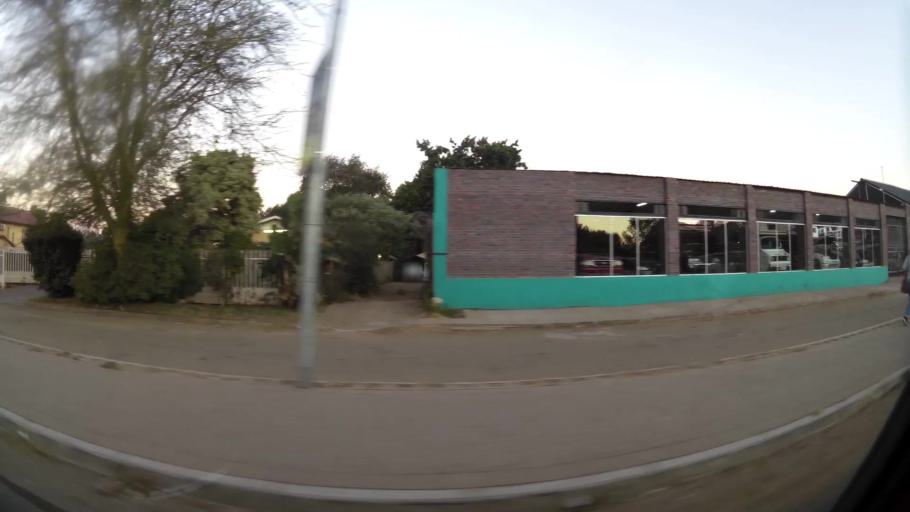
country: ZA
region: North-West
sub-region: Bojanala Platinum District Municipality
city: Rustenburg
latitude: -25.6573
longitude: 27.2426
